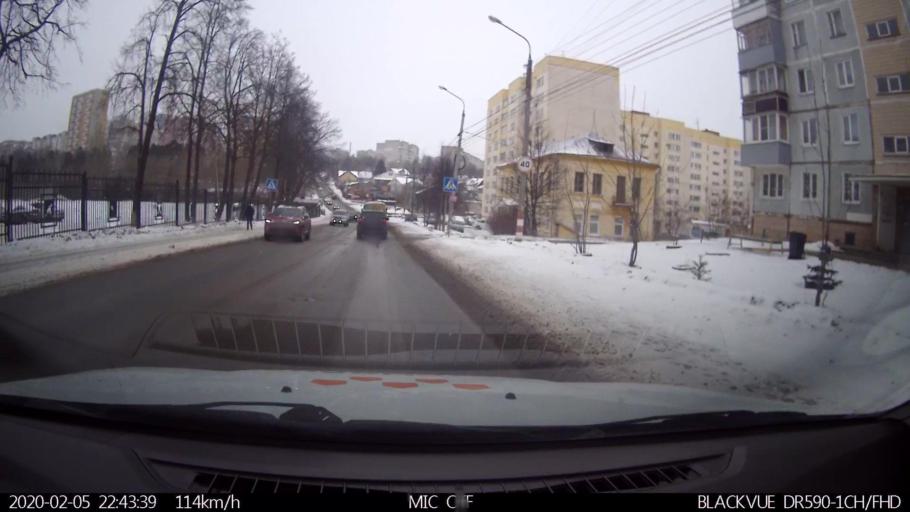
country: RU
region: Nizjnij Novgorod
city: Imeni Stepana Razina
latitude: 54.7118
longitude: 44.3833
